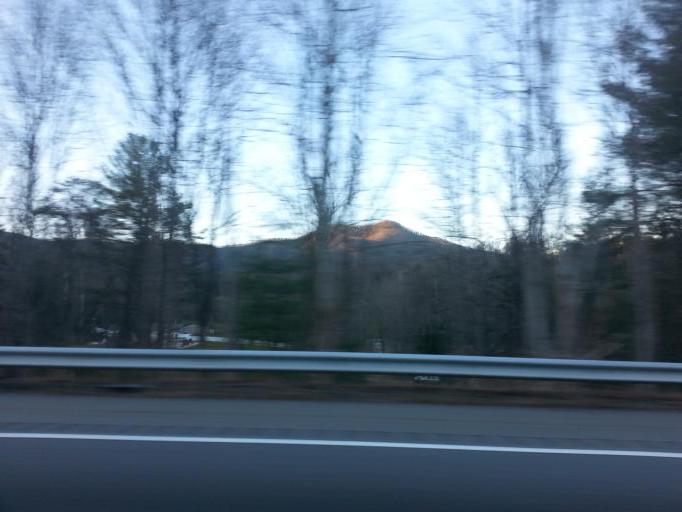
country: US
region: North Carolina
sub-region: Haywood County
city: Canton
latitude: 35.5518
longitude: -82.7305
